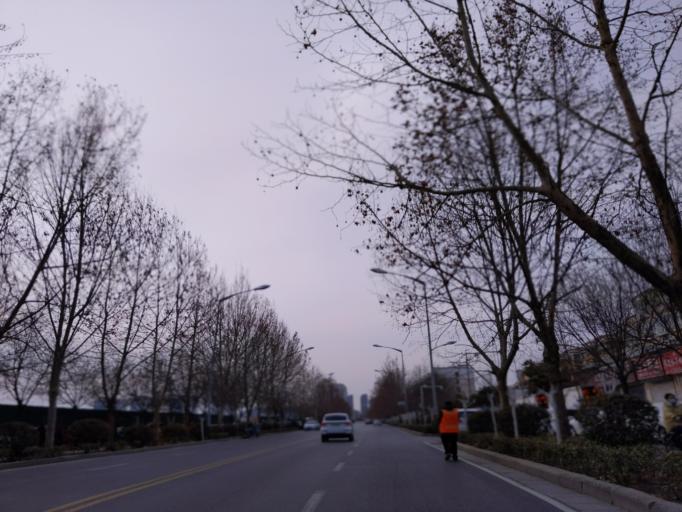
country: CN
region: Henan Sheng
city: Zhongyuanlu
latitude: 35.7578
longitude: 115.0507
